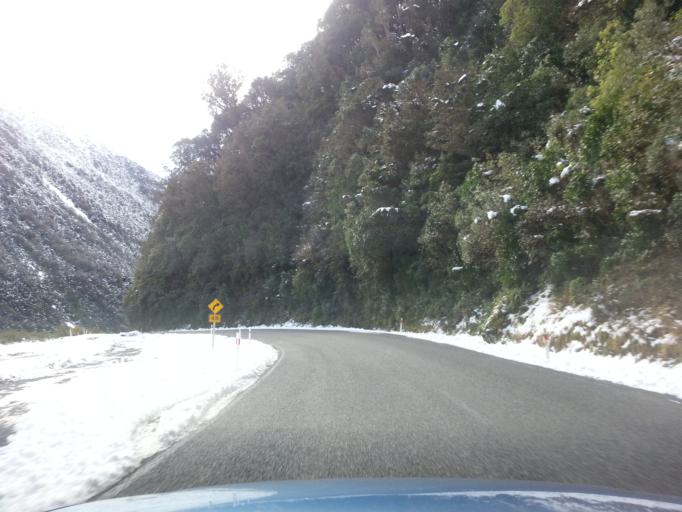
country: NZ
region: West Coast
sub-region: Grey District
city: Greymouth
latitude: -42.8572
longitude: 171.5599
